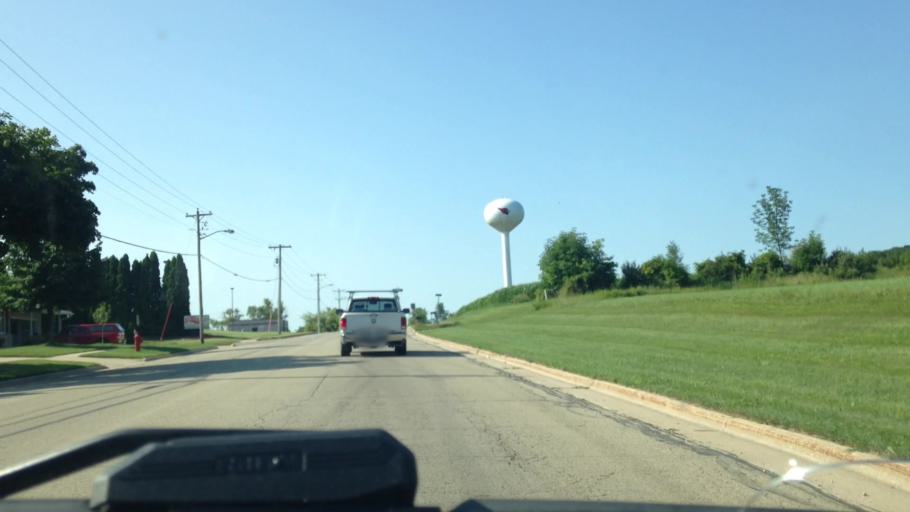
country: US
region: Wisconsin
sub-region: Dodge County
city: Mayville
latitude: 43.4906
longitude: -88.5562
